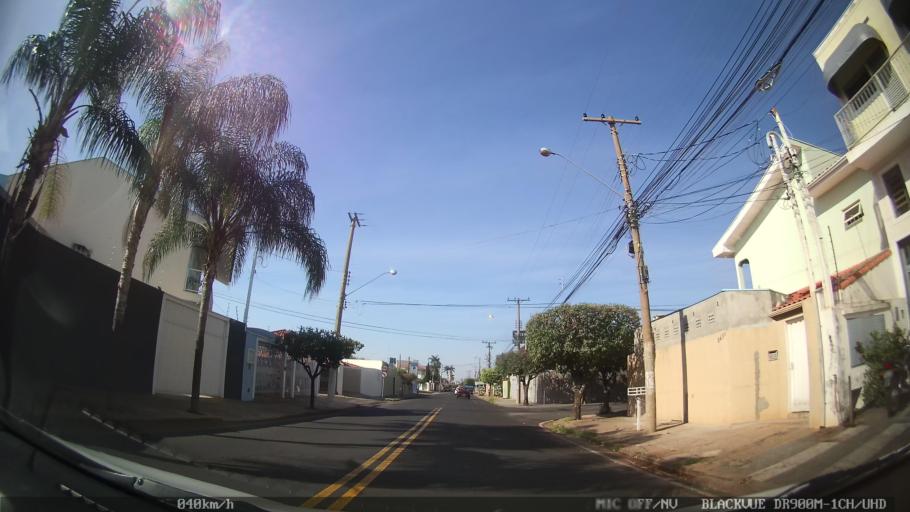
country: BR
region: Sao Paulo
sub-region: Sao Jose Do Rio Preto
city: Sao Jose do Rio Preto
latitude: -20.8083
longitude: -49.3954
